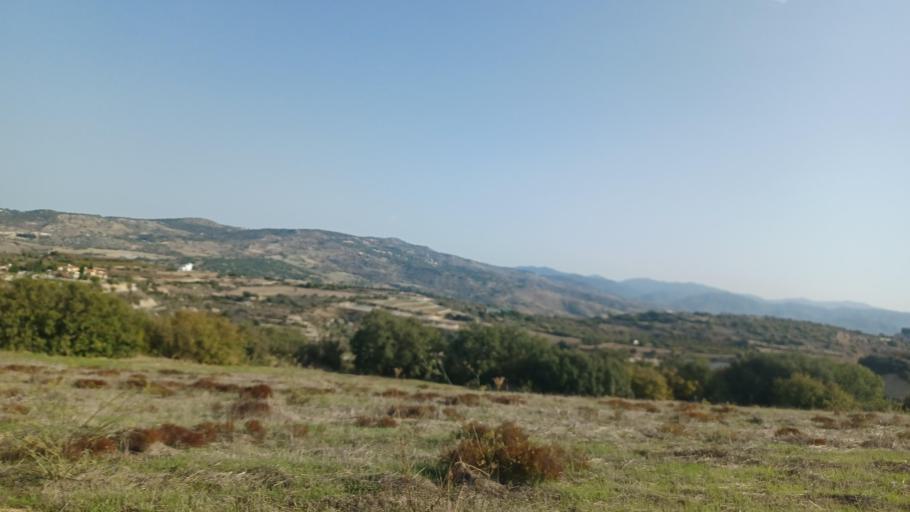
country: CY
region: Pafos
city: Polis
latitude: 34.9462
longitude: 32.4778
